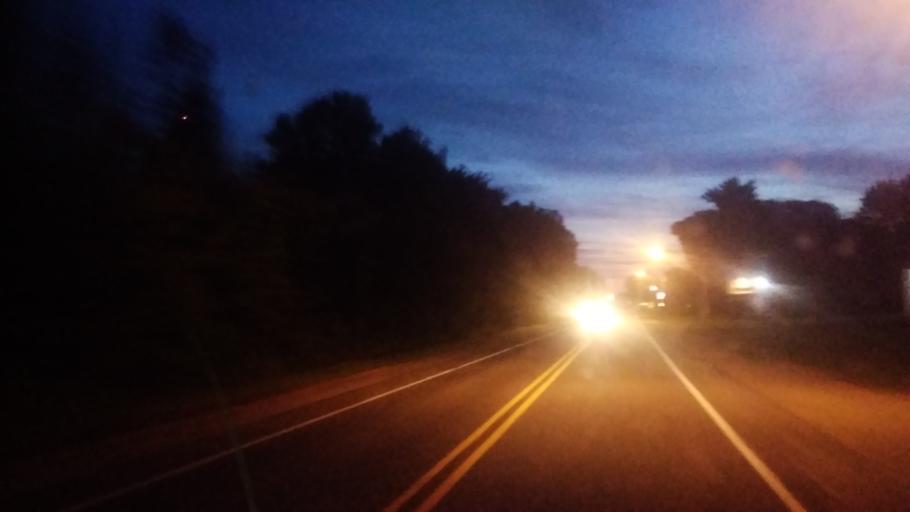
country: US
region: Michigan
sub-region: Kent County
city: Cedar Springs
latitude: 43.2888
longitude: -85.5166
